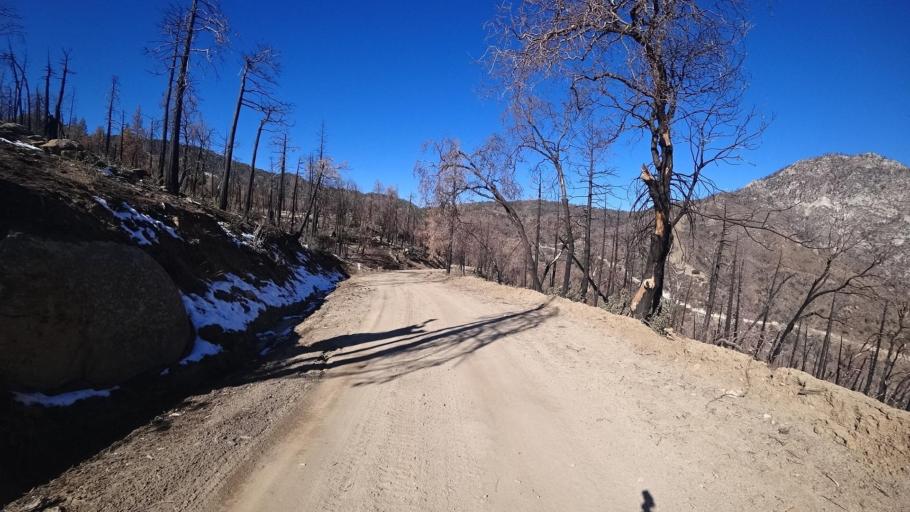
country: US
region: California
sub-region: Kern County
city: Alta Sierra
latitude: 35.7172
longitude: -118.5290
